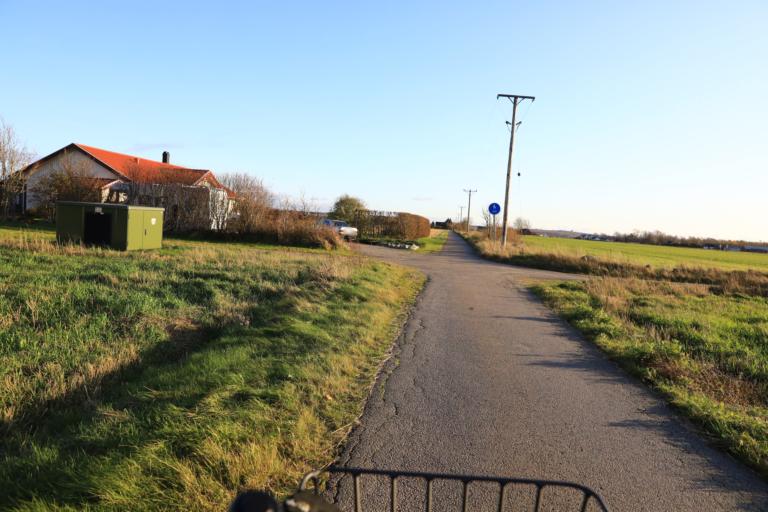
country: SE
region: Halland
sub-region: Varbergs Kommun
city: Varberg
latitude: 57.1536
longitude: 12.2422
